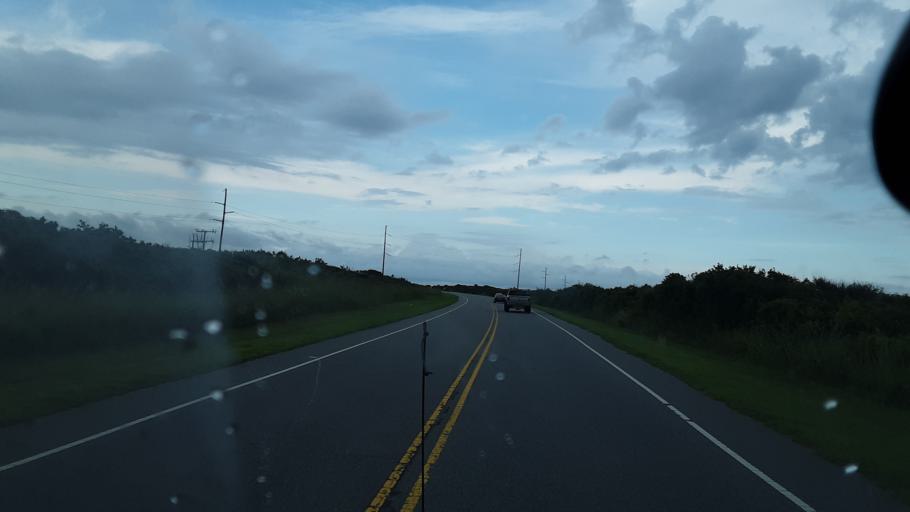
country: US
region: North Carolina
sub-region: Dare County
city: Wanchese
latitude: 35.8408
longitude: -75.5632
